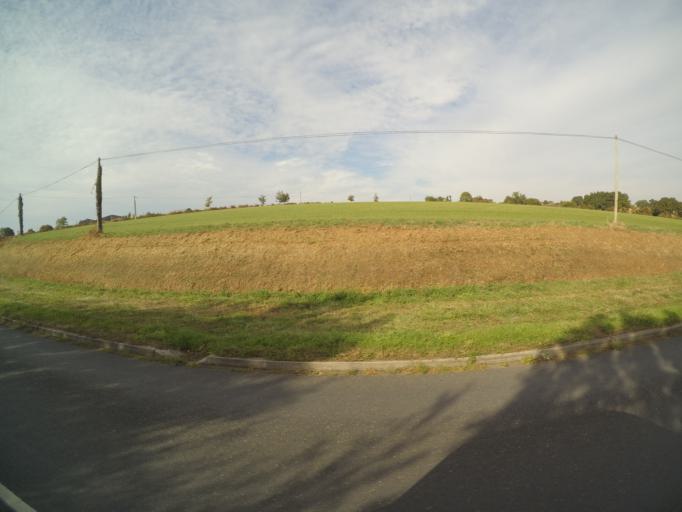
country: FR
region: Pays de la Loire
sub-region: Departement de Maine-et-Loire
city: La Chapelle-du-Genet
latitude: 47.1876
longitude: -1.0341
